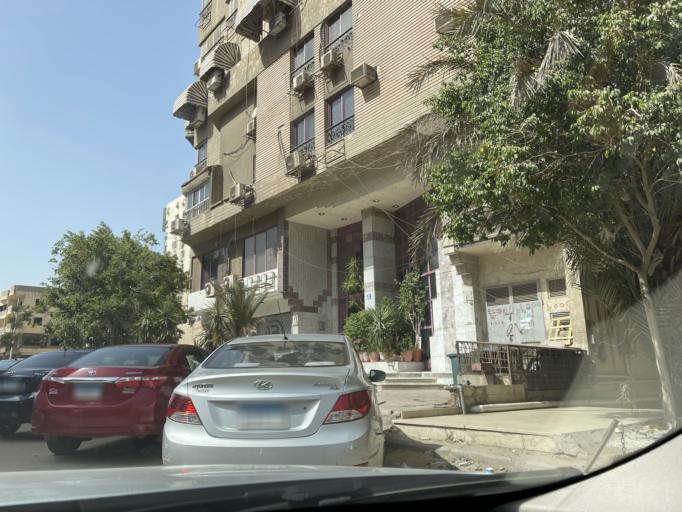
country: EG
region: Muhafazat al Qahirah
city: Cairo
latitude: 30.0685
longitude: 31.3554
